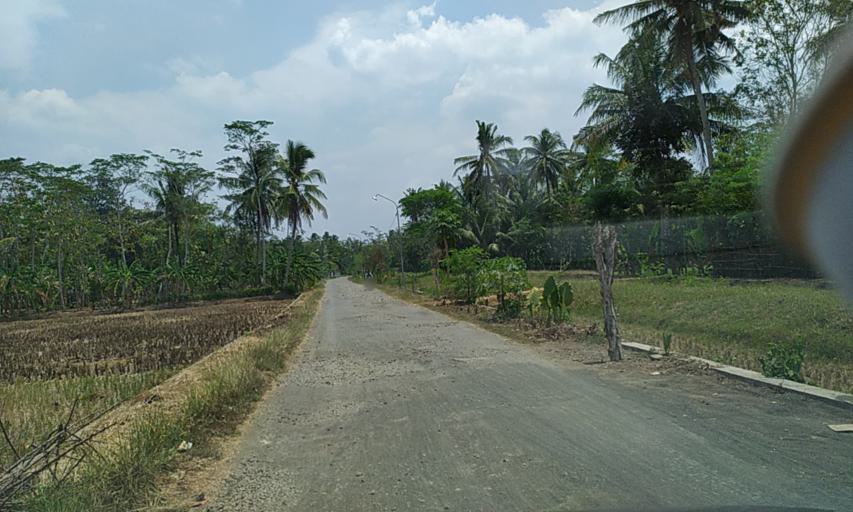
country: ID
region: Central Java
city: Kedungreja
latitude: -7.5015
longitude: 108.7799
